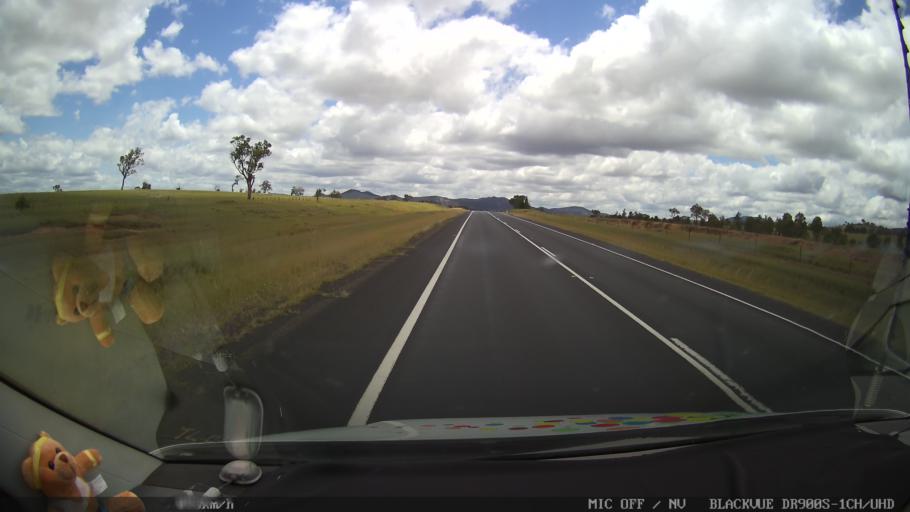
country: AU
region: New South Wales
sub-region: Glen Innes Severn
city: Glen Innes
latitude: -29.3953
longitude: 151.8790
